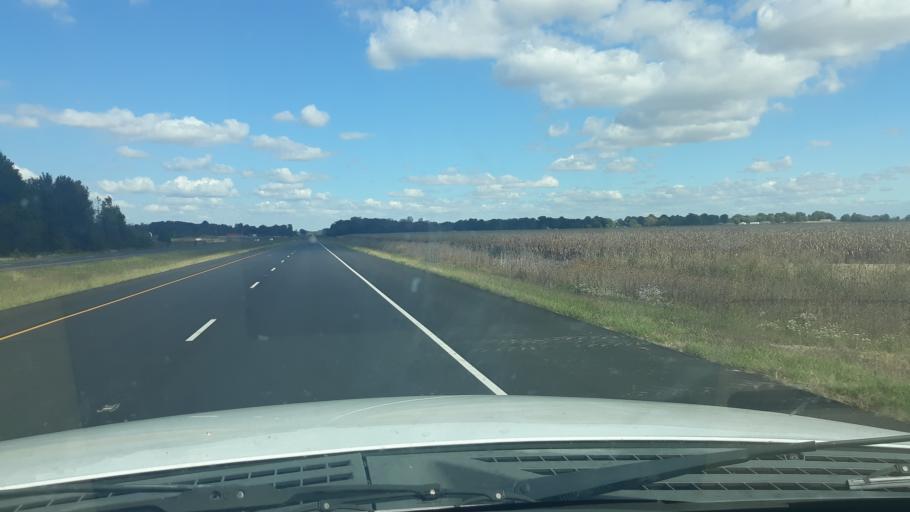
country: US
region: Illinois
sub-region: Saline County
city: Harrisburg
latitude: 37.7789
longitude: -88.4985
